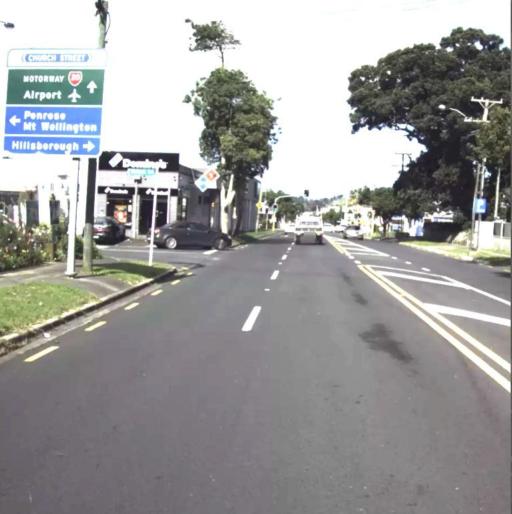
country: NZ
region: Auckland
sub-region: Auckland
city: Mangere
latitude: -36.9219
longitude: 174.7830
